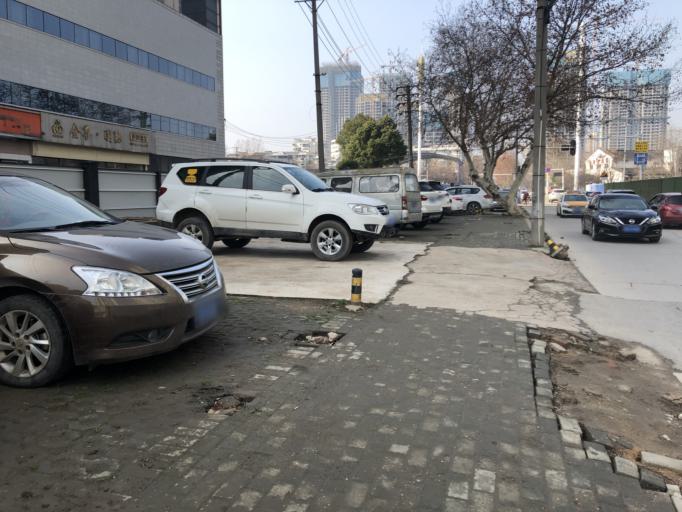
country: CN
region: Hubei
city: Jiang'an
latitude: 30.6032
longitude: 114.3497
